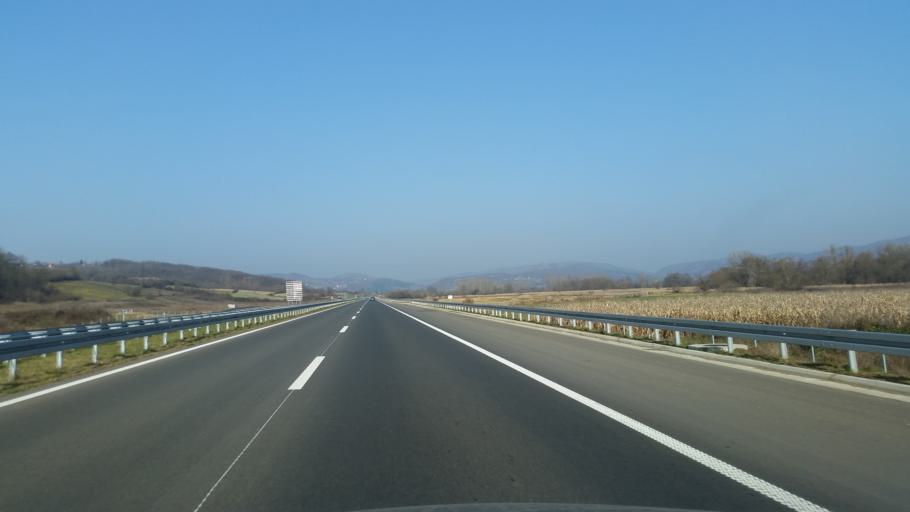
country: RS
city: Prislonica
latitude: 43.9320
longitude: 20.4015
